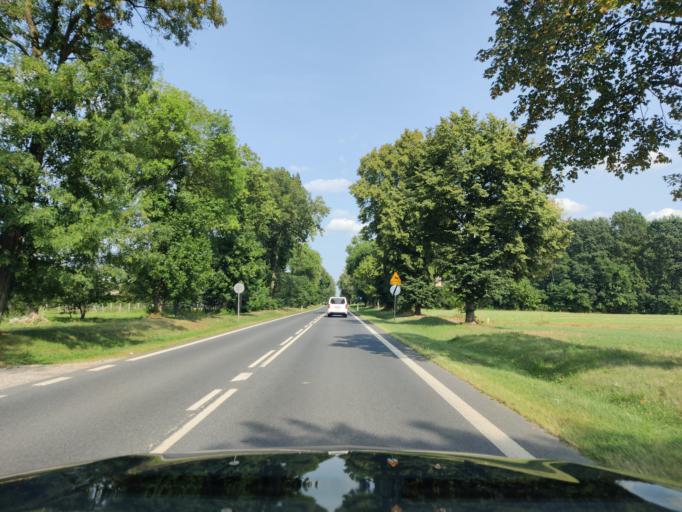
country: PL
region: Masovian Voivodeship
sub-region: Powiat makowski
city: Rzewnie
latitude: 52.8496
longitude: 21.2843
